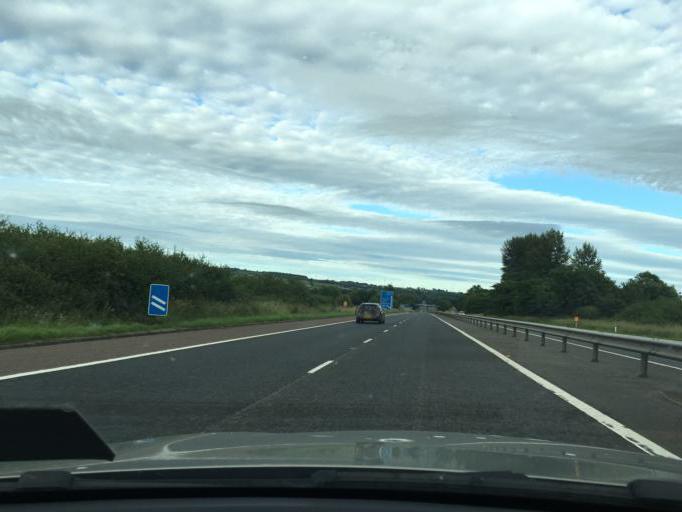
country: GB
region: Northern Ireland
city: Randalstown
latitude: 54.7445
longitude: -6.2490
